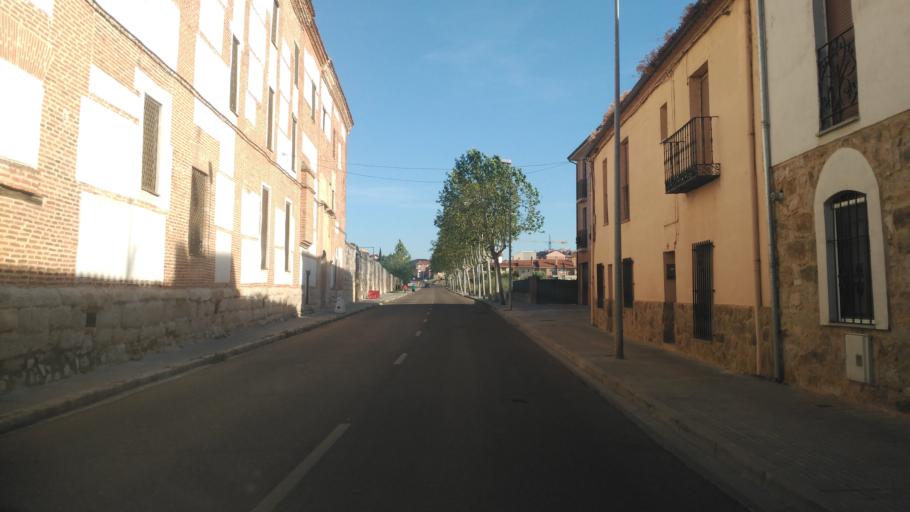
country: ES
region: Castille and Leon
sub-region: Provincia de Zamora
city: Zamora
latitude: 41.4963
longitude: -5.7471
